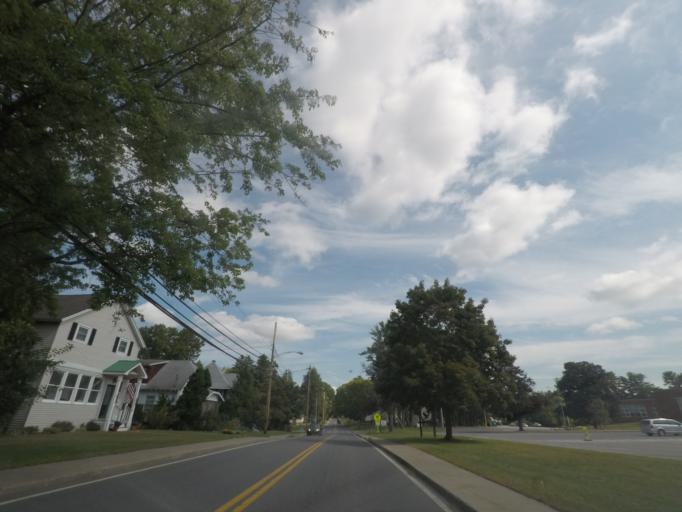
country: US
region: New York
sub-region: Albany County
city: Delmar
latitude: 42.6212
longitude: -73.8263
